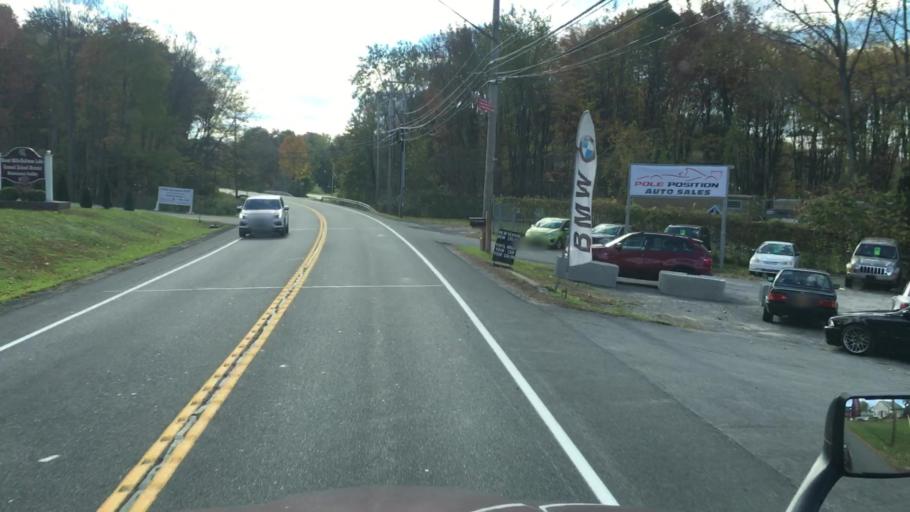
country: US
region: New York
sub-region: Schenectady County
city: East Glenville
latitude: 42.9166
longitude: -73.8928
